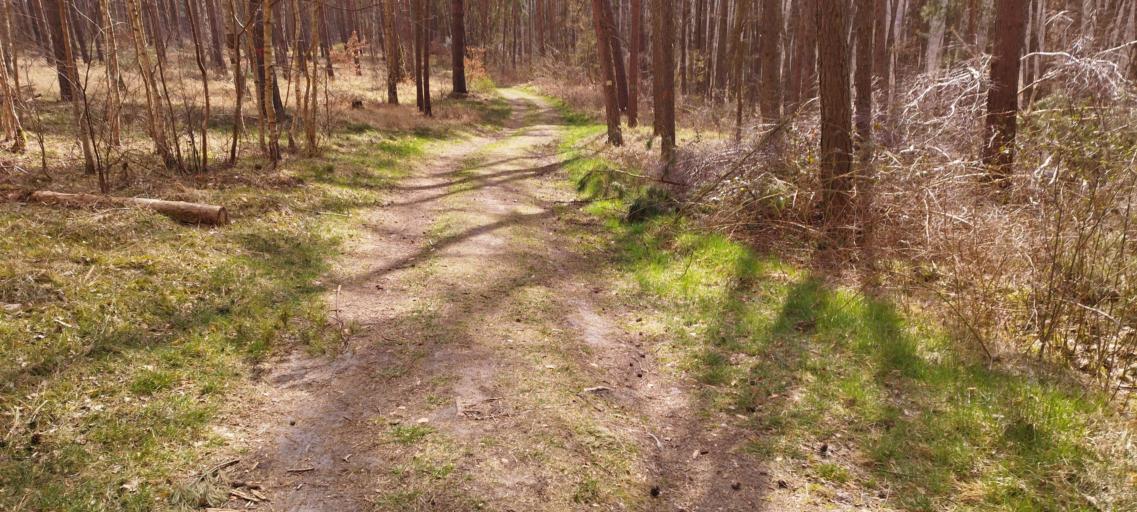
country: DE
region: Brandenburg
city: Grunheide
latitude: 52.4110
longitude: 13.8555
